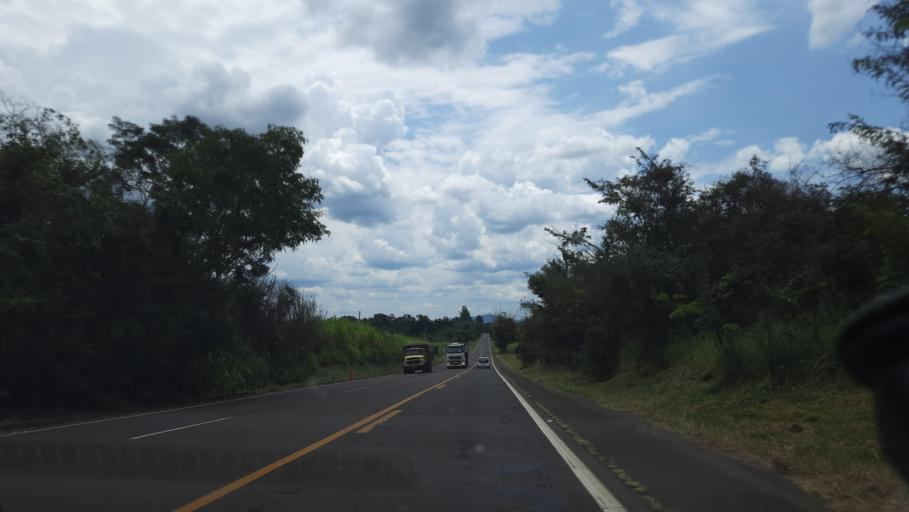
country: BR
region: Sao Paulo
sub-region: Mococa
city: Mococa
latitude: -21.4757
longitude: -47.0896
